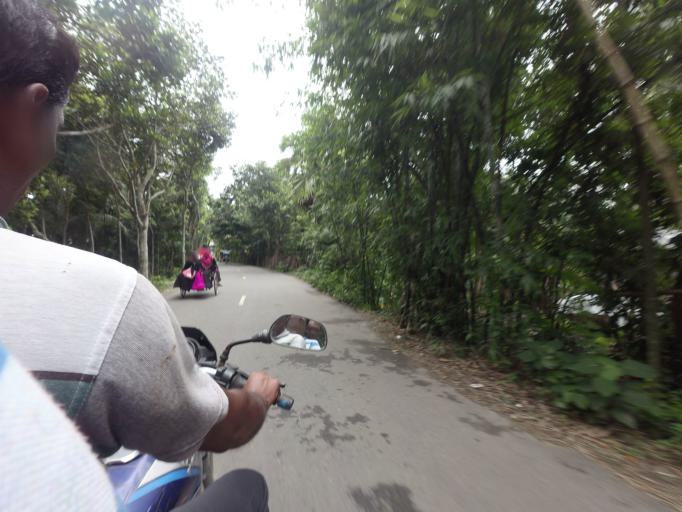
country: BD
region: Khulna
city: Kalia
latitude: 23.1660
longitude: 89.6455
